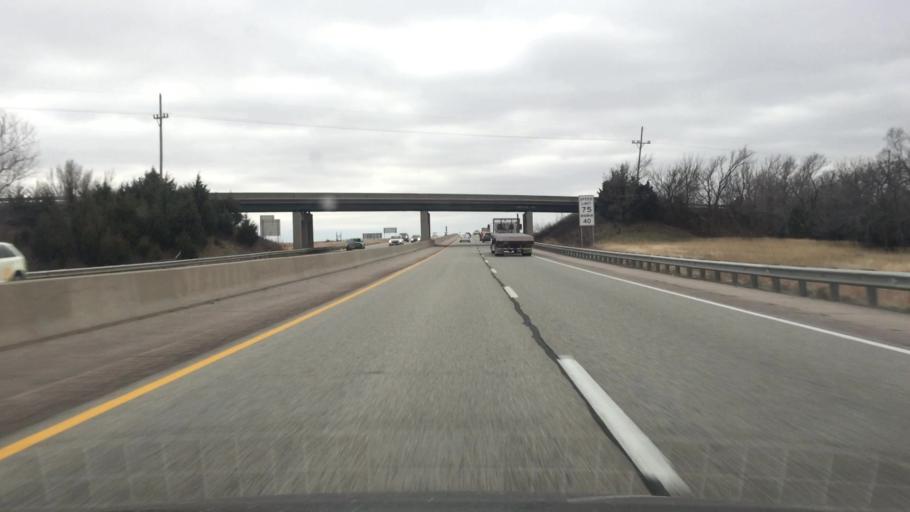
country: US
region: Kansas
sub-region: Butler County
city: El Dorado
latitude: 38.0436
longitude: -96.6445
